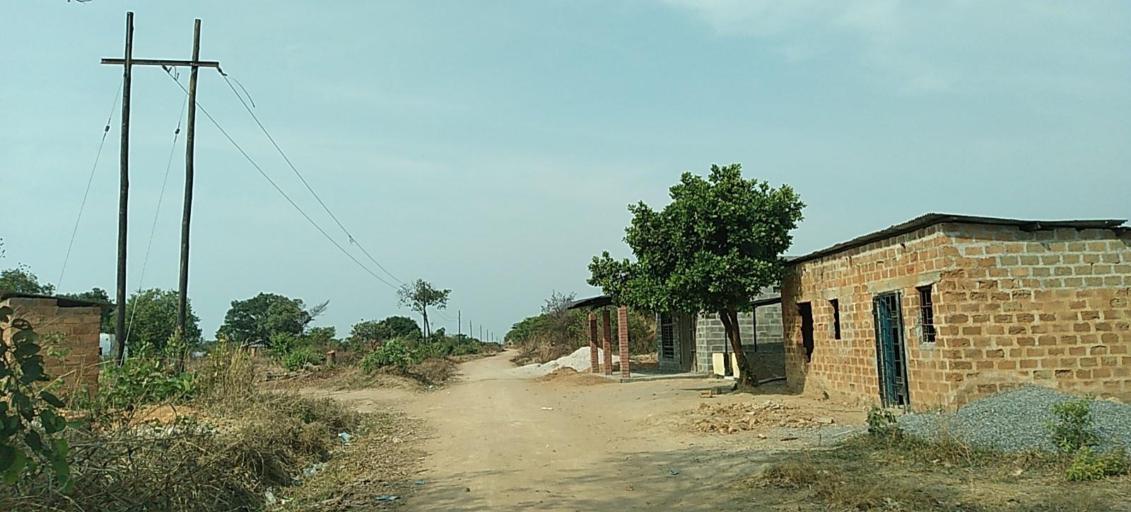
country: ZM
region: Copperbelt
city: Ndola
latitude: -13.2188
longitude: 28.6808
